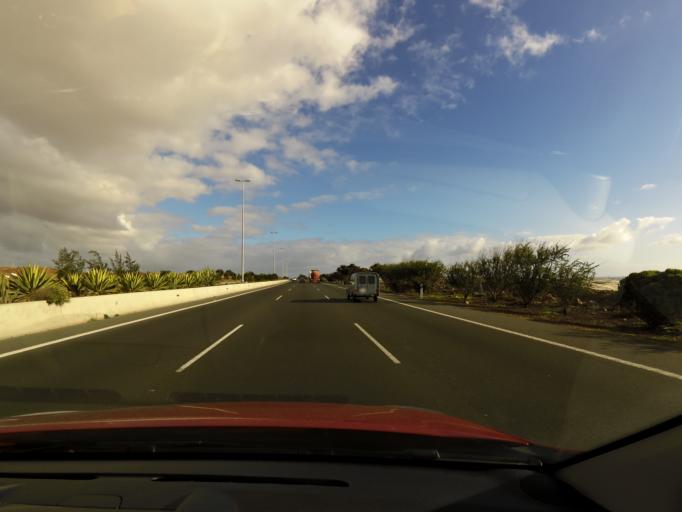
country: ES
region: Canary Islands
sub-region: Provincia de Las Palmas
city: Cruce de Arinaga
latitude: 27.9019
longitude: -15.4026
